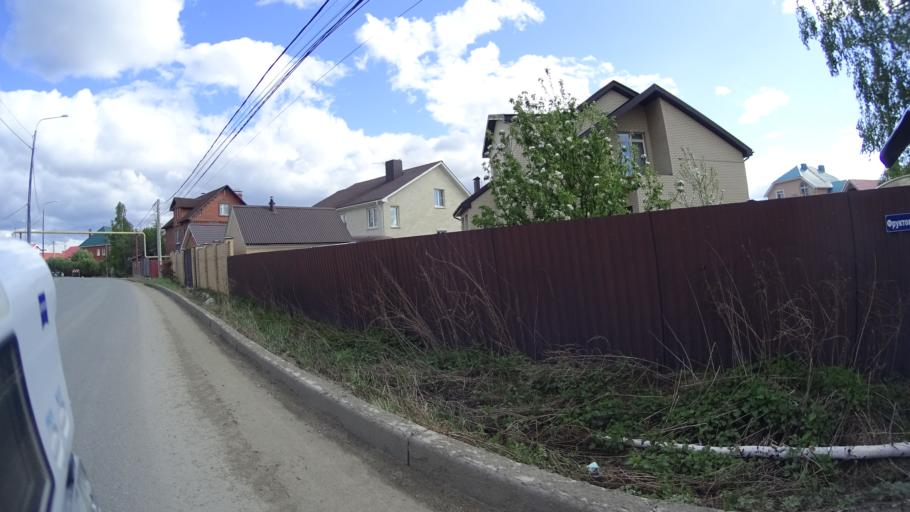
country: RU
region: Chelyabinsk
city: Sargazy
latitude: 55.1527
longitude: 61.2553
